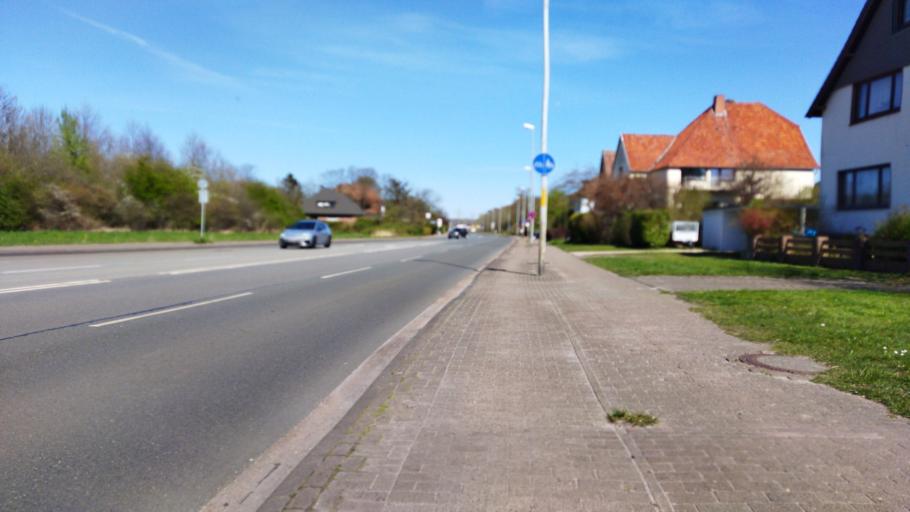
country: DE
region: Lower Saxony
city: Nordenham
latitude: 53.5221
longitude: 8.5187
